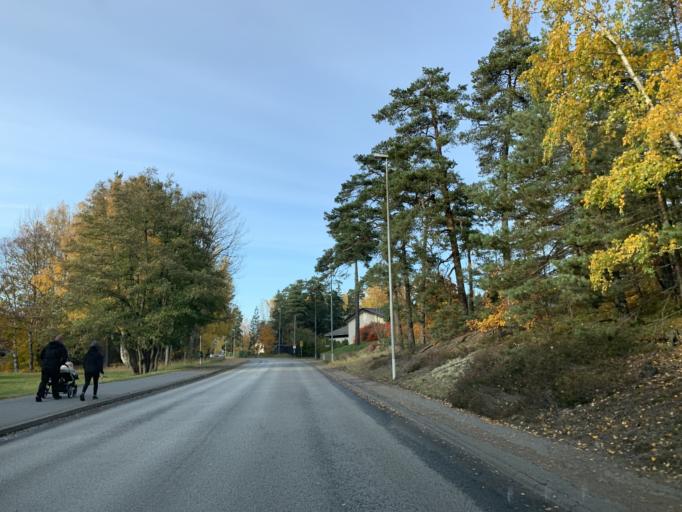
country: SE
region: Stockholm
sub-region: Haninge Kommun
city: Haninge
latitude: 59.1771
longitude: 18.1829
